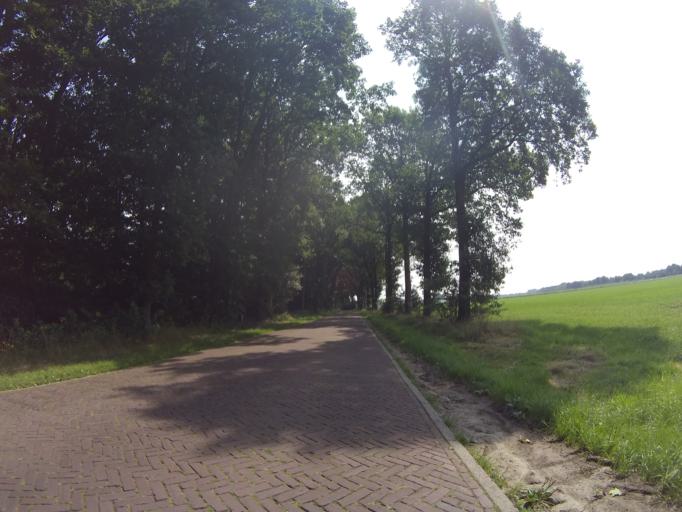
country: NL
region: Drenthe
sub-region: Gemeente Coevorden
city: Sleen
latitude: 52.7979
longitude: 6.6944
